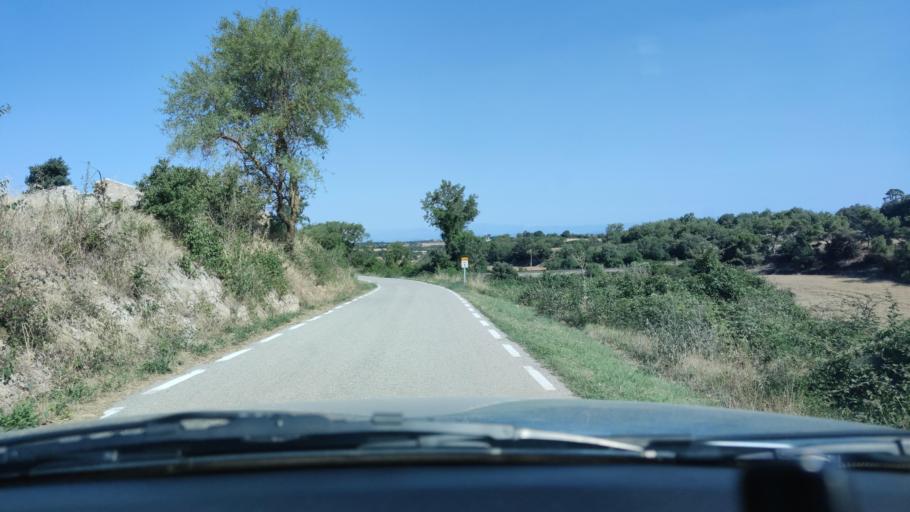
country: ES
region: Catalonia
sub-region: Provincia de Lleida
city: Sant Guim de Freixenet
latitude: 41.6476
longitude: 1.4095
